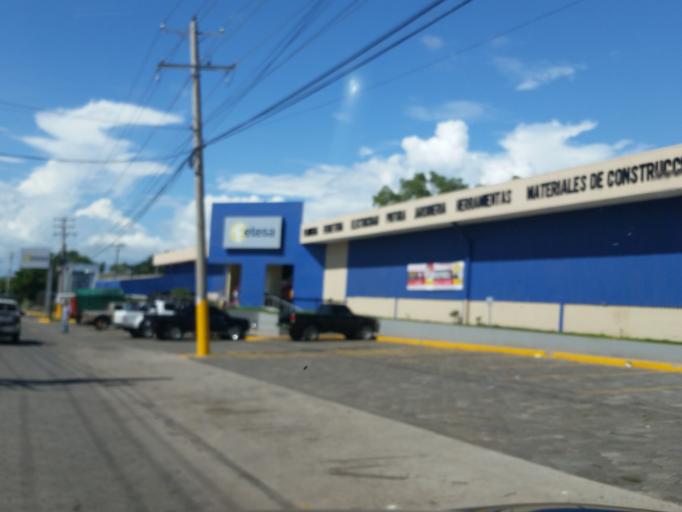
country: NI
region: Managua
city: Managua
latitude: 12.1601
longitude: -86.2237
